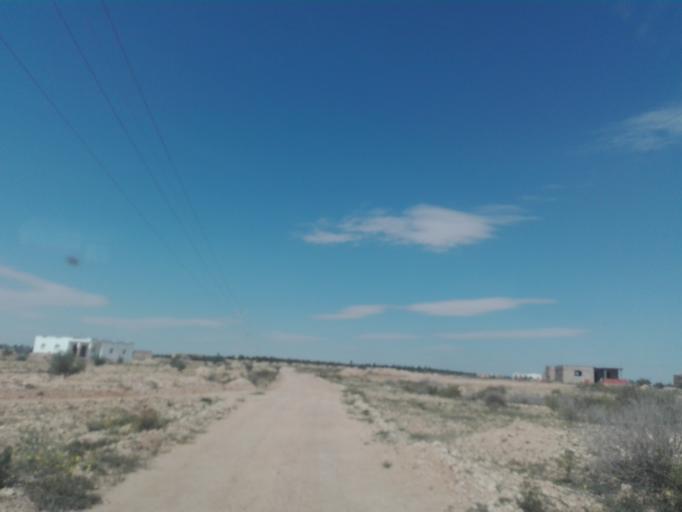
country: TN
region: Safaqis
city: Sfax
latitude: 34.6882
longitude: 10.5343
